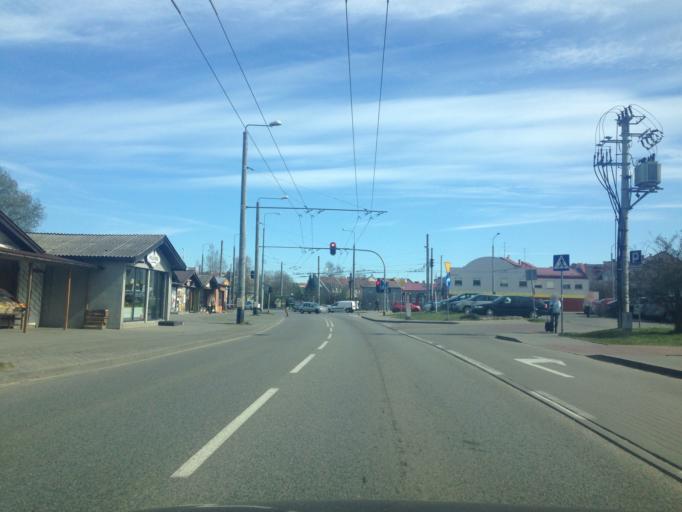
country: PL
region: Pomeranian Voivodeship
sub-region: Gdynia
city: Wielki Kack
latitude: 54.4744
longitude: 18.4643
